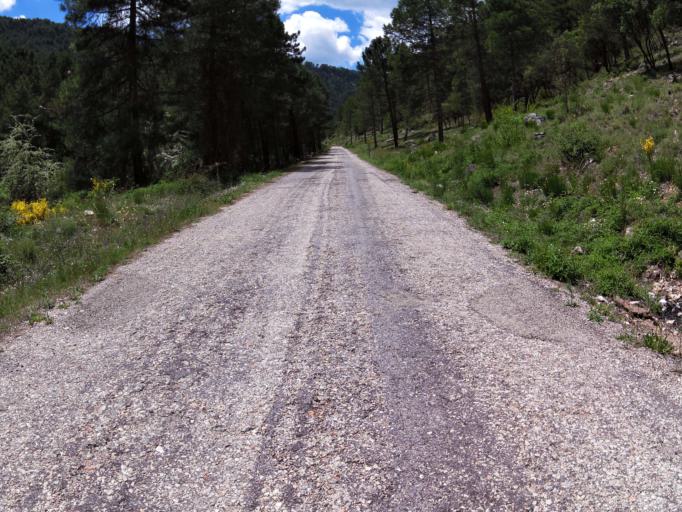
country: ES
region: Castille-La Mancha
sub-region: Provincia de Albacete
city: Paterna del Madera
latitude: 38.5737
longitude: -2.3553
